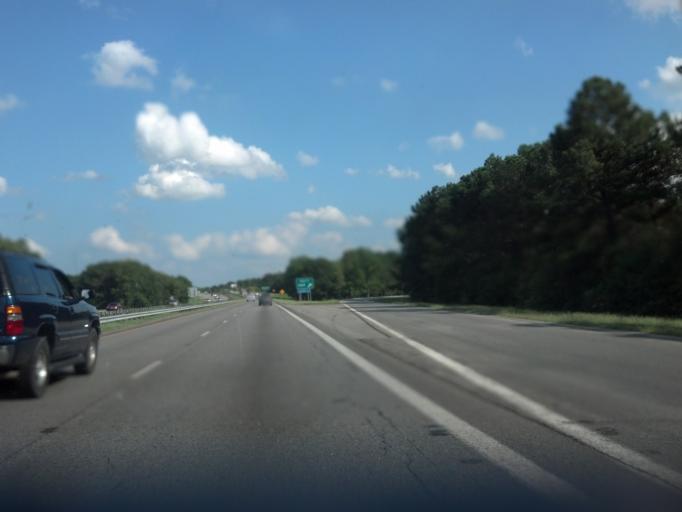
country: US
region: North Carolina
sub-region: Nash County
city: Rocky Mount
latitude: 35.9621
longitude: -77.7962
